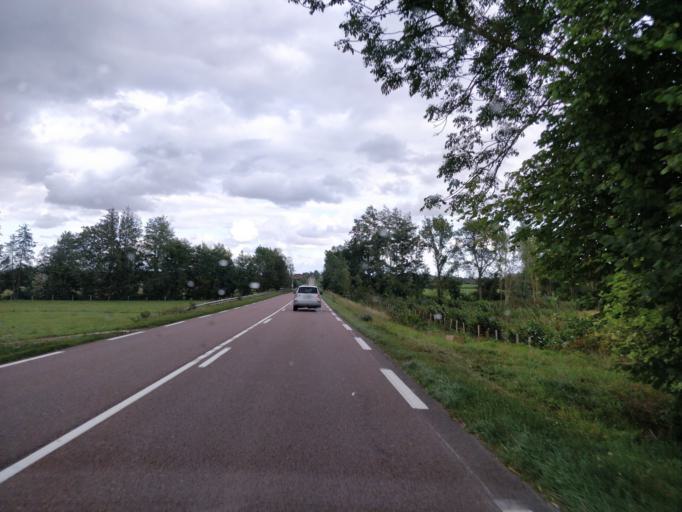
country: FR
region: Champagne-Ardenne
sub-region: Departement de l'Aube
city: Lusigny-sur-Barse
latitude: 48.2433
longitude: 4.2845
